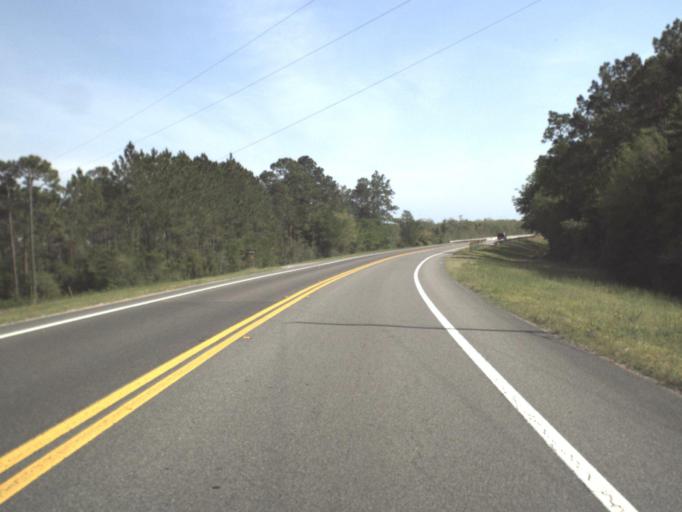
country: US
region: Florida
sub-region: Santa Rosa County
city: East Milton
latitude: 30.5840
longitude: -86.9305
